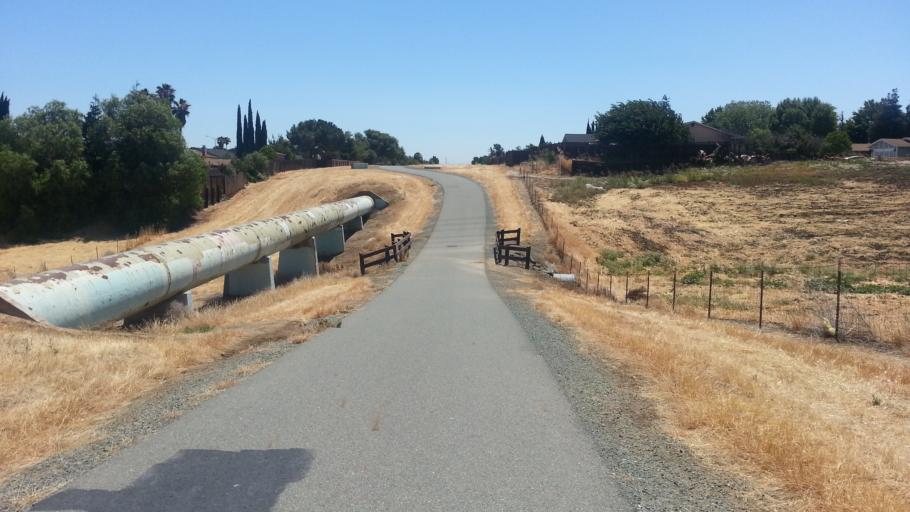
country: US
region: California
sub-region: Contra Costa County
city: Bay Point
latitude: 38.0179
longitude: -121.9246
